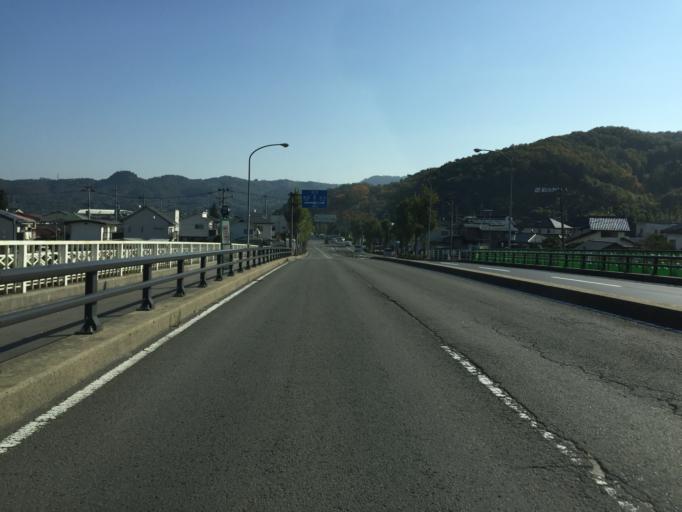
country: JP
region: Fukushima
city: Fukushima-shi
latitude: 37.7716
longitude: 140.4937
